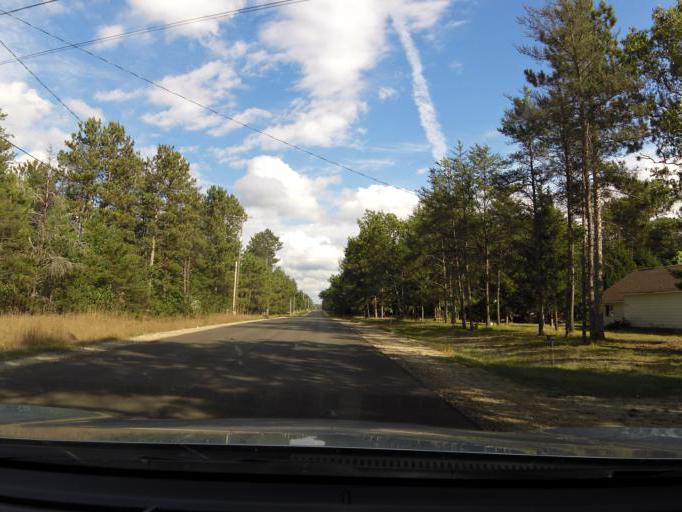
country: US
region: Michigan
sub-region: Roscommon County
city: Roscommon
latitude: 44.5256
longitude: -84.5695
